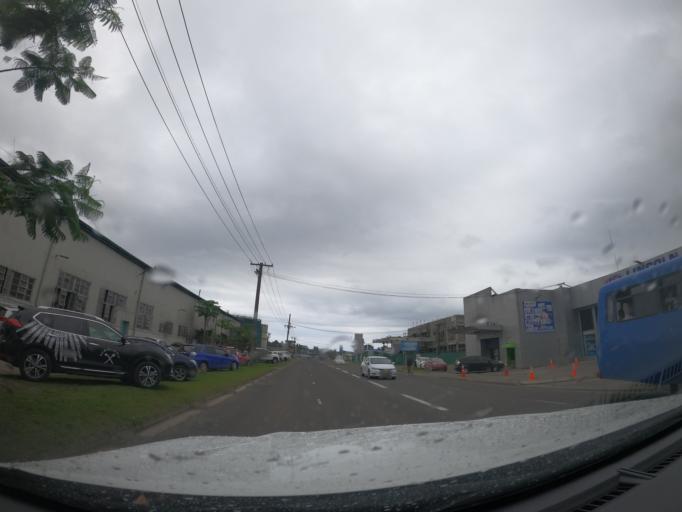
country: FJ
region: Central
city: Suva
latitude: -18.1271
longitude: 178.4308
